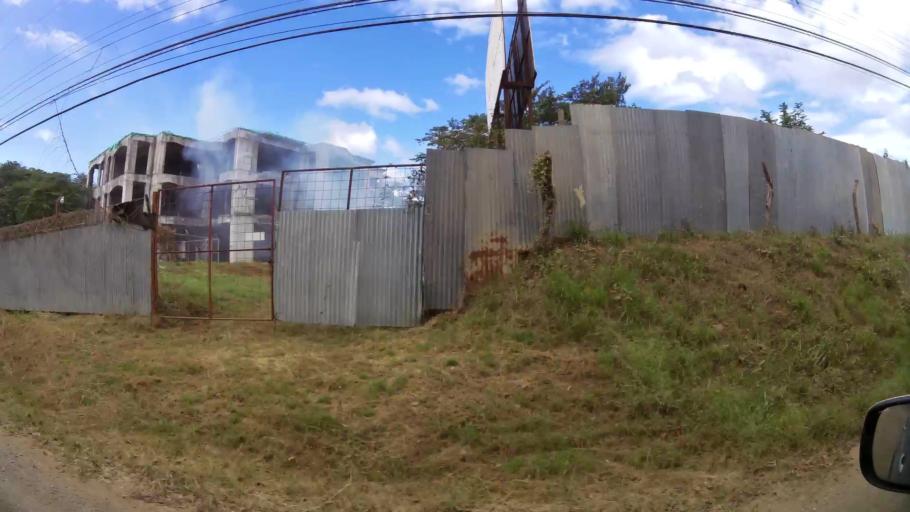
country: CR
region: Guanacaste
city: Santa Cruz
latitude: 10.2910
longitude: -85.8492
